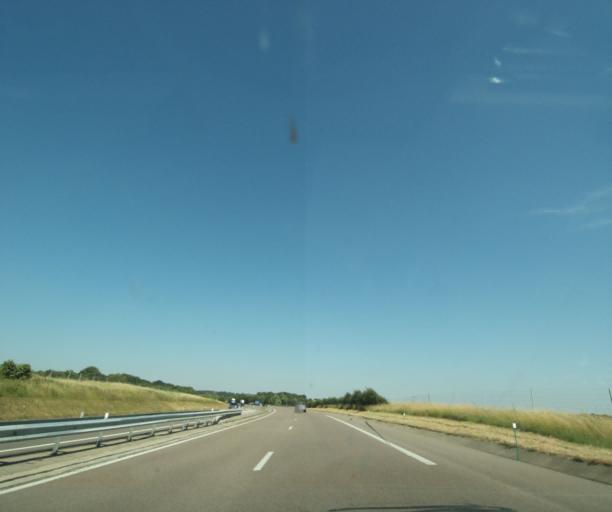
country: FR
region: Lorraine
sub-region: Departement des Vosges
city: Chatenois
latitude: 48.4041
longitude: 5.8781
